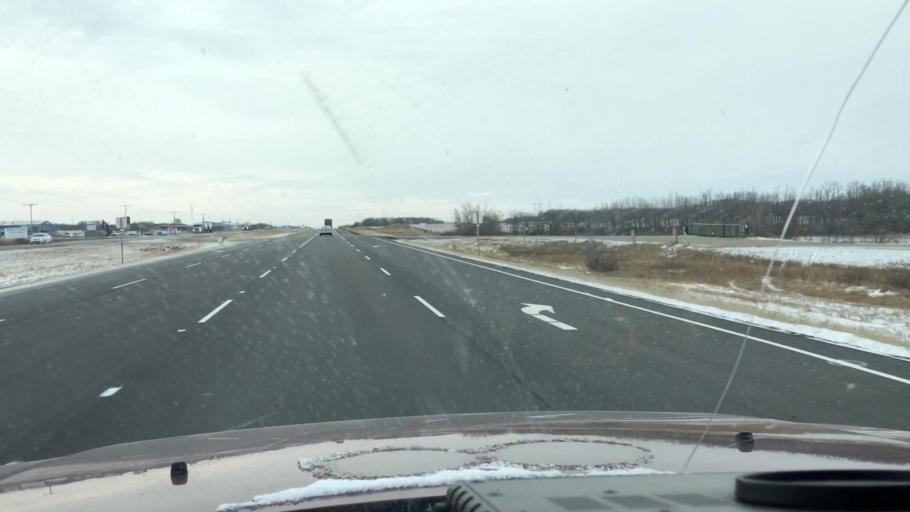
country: CA
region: Saskatchewan
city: Saskatoon
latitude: 51.9701
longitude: -106.5541
